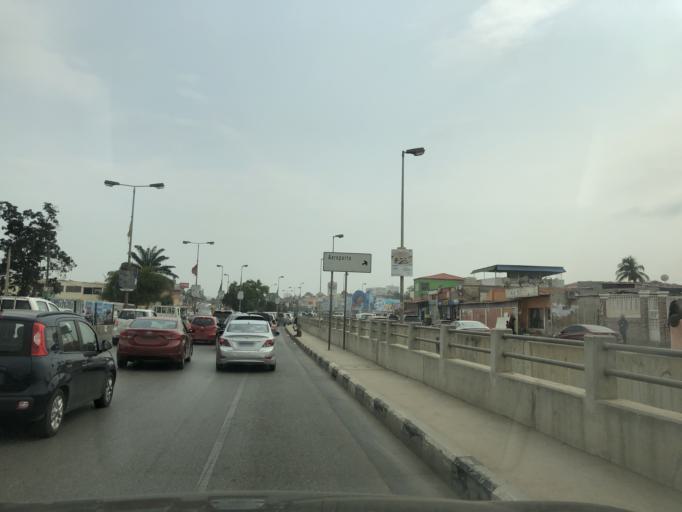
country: AO
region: Luanda
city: Luanda
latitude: -8.8494
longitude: 13.2107
